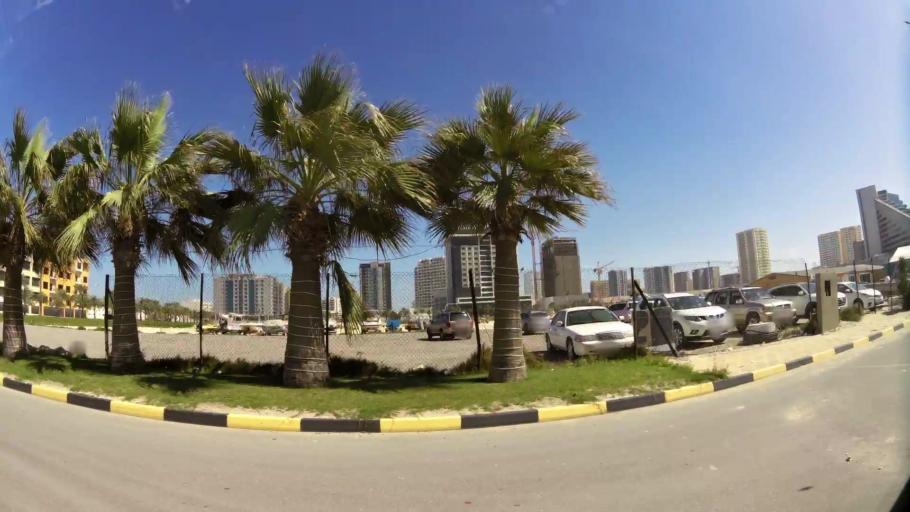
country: BH
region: Muharraq
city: Al Hadd
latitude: 26.2929
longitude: 50.6597
